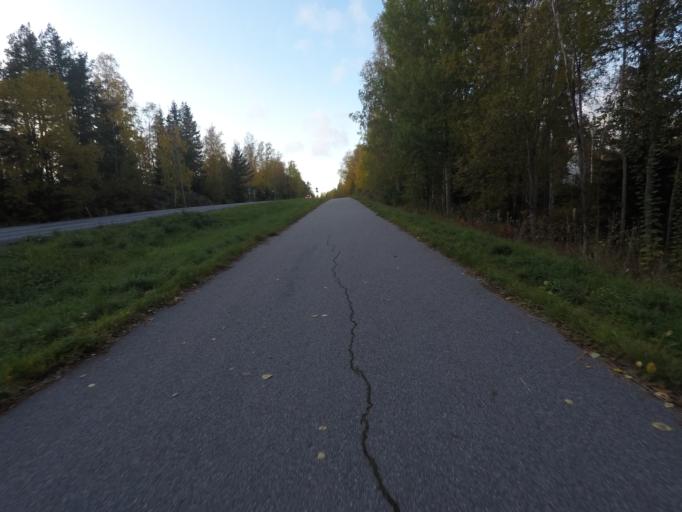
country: SE
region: OErebro
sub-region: Karlskoga Kommun
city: Karlskoga
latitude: 59.3036
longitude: 14.4920
